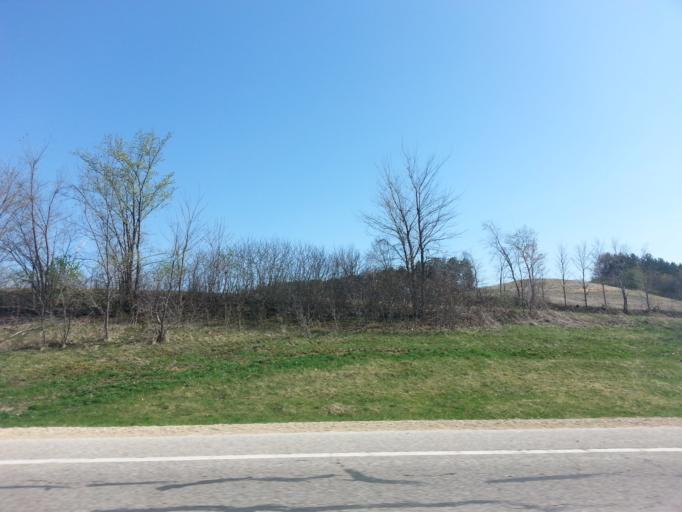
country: US
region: Wisconsin
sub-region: Pepin County
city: Durand
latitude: 44.6423
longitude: -92.0457
